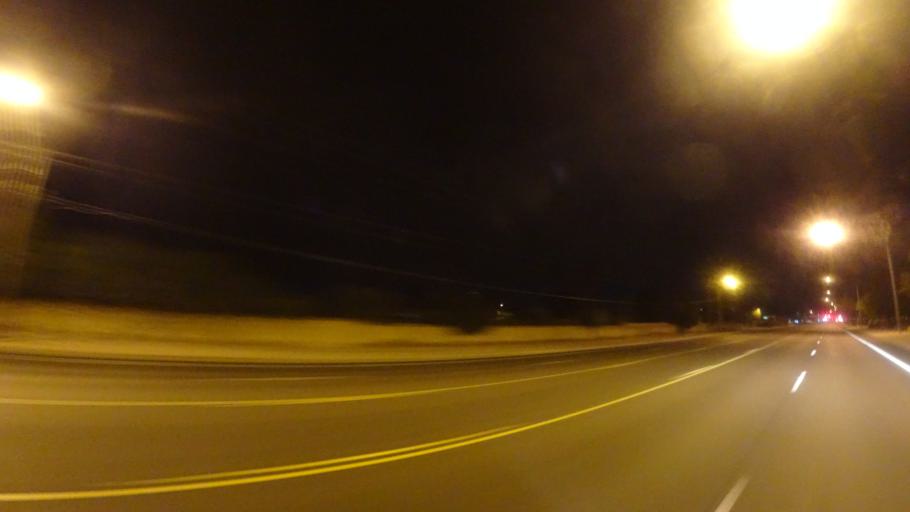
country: US
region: Arizona
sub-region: Maricopa County
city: Mesa
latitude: 33.4423
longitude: -111.7017
